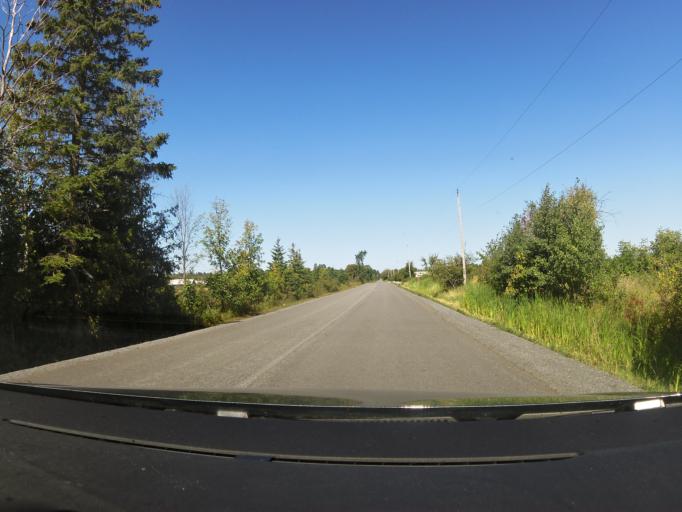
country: CA
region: Ontario
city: Bells Corners
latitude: 45.2600
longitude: -76.0001
